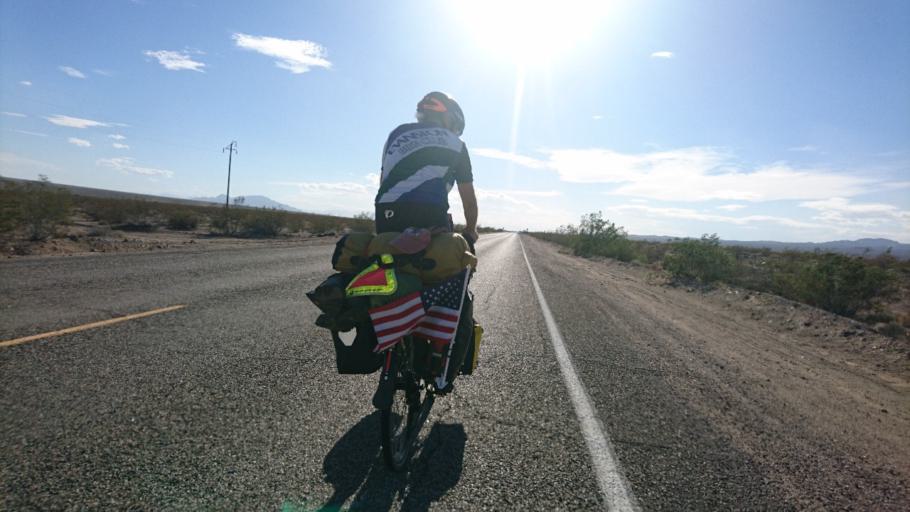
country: US
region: California
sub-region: San Bernardino County
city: Needles
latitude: 34.7136
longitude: -115.2795
